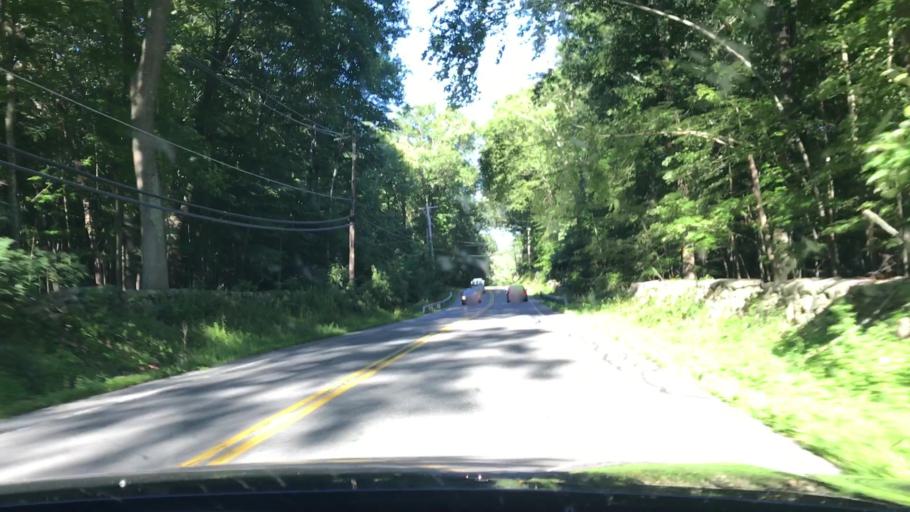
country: US
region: New York
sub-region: Westchester County
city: Heritage Hills
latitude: 41.3686
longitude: -73.6934
